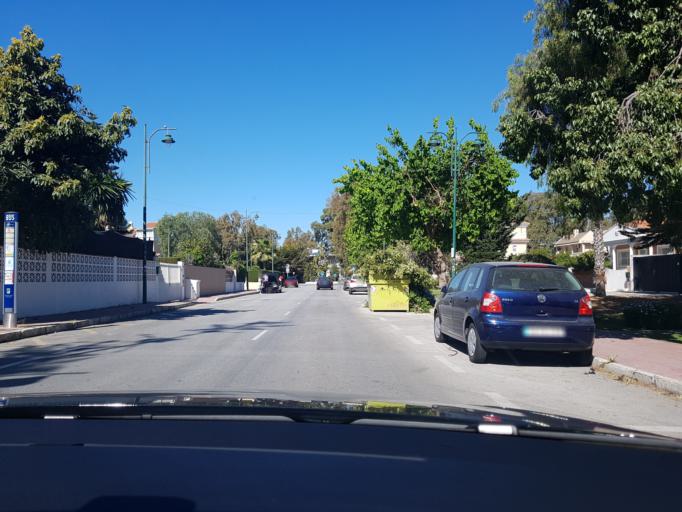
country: ES
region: Andalusia
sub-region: Provincia de Malaga
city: Torremolinos
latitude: 36.6684
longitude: -4.4638
